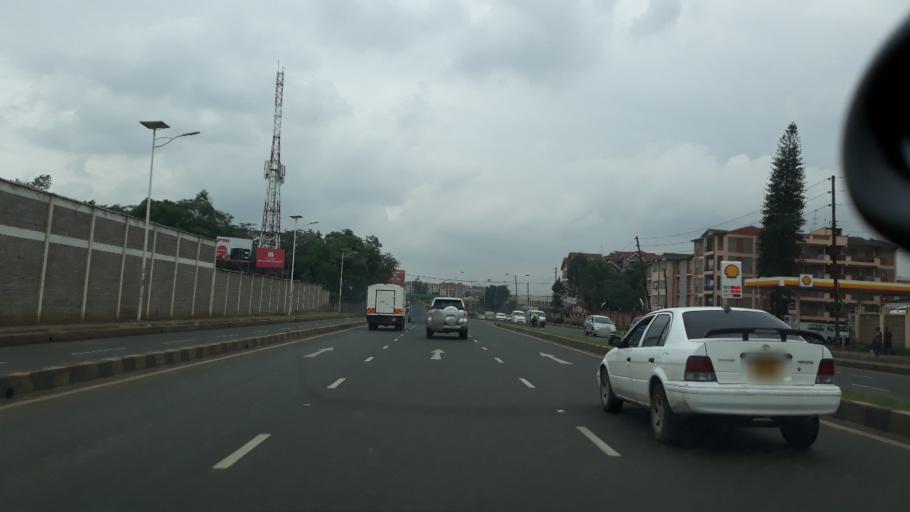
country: KE
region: Nairobi Area
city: Nairobi
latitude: -1.2675
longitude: 36.8304
